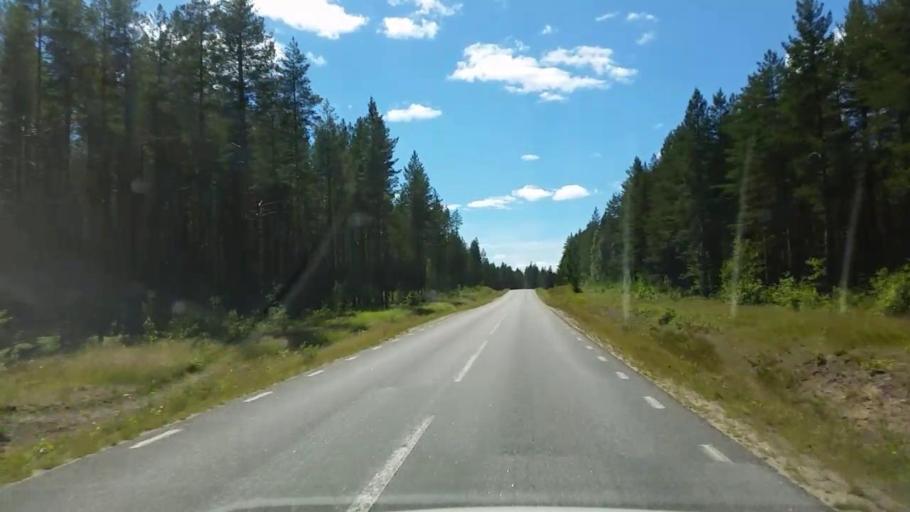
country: SE
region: Gaevleborg
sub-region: Ljusdals Kommun
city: Farila
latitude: 61.7545
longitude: 15.7737
